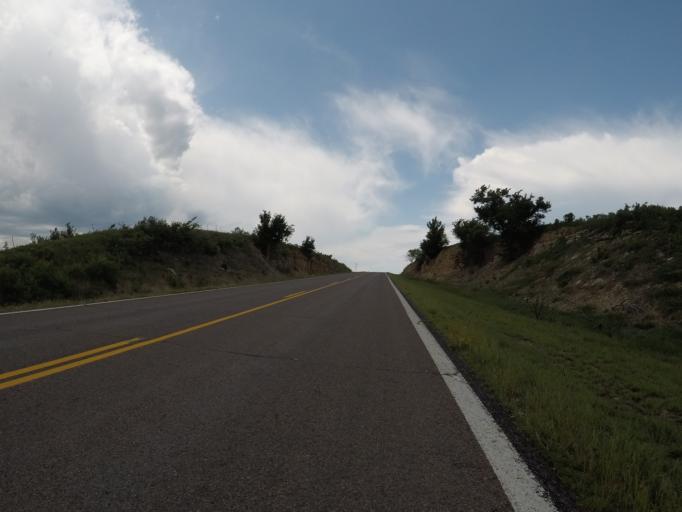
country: US
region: Kansas
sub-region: Wabaunsee County
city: Alma
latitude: 38.8704
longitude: -96.3610
